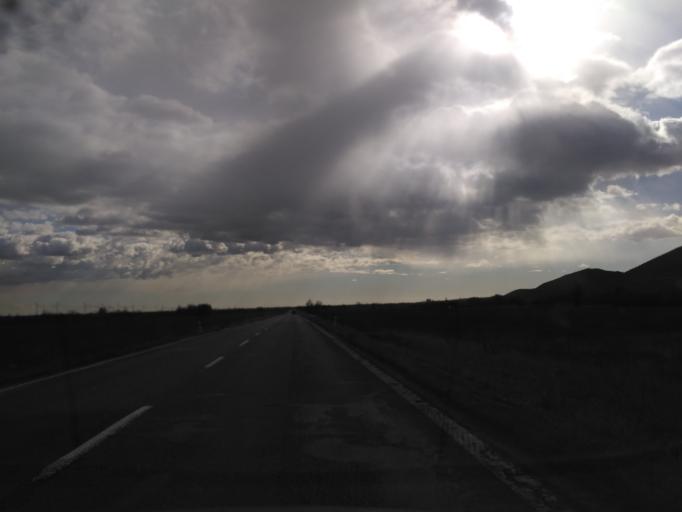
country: HU
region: Borsod-Abauj-Zemplen
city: Satoraljaujhely
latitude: 48.4398
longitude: 21.6553
